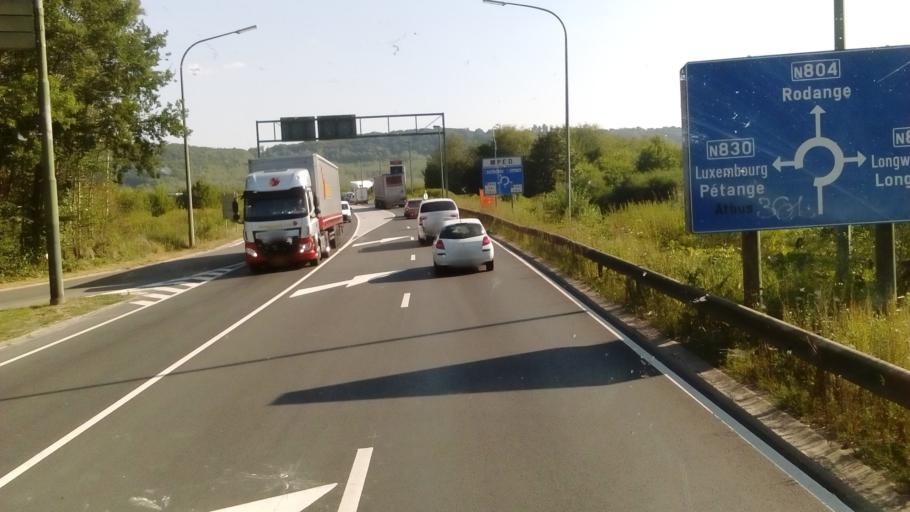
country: BE
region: Wallonia
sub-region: Province du Luxembourg
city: Aubange
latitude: 49.5518
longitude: 5.8102
